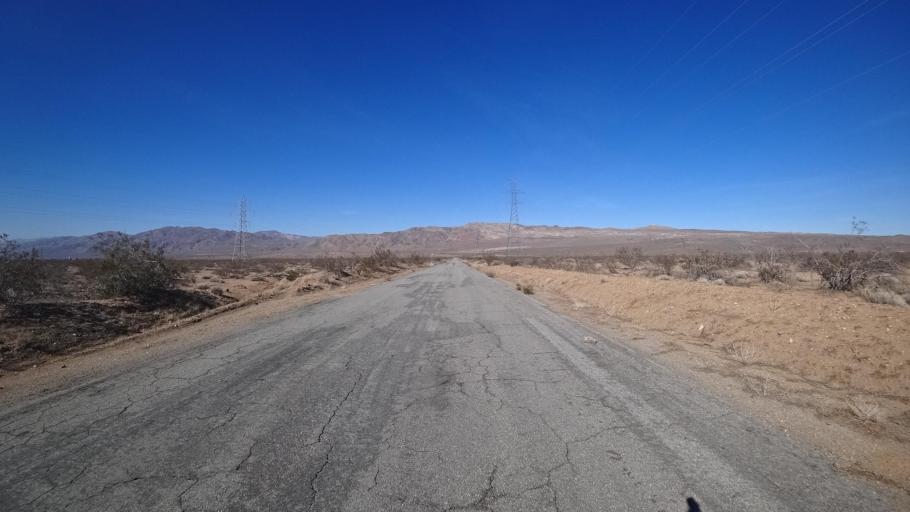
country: US
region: California
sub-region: Kern County
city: Ridgecrest
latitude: 35.4015
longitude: -117.6769
